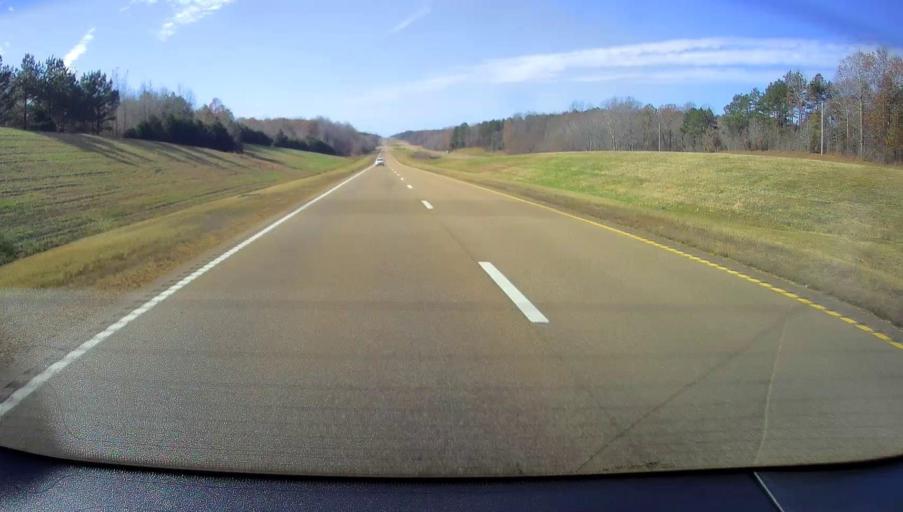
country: US
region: Mississippi
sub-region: Benton County
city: Ashland
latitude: 34.9529
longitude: -89.0481
